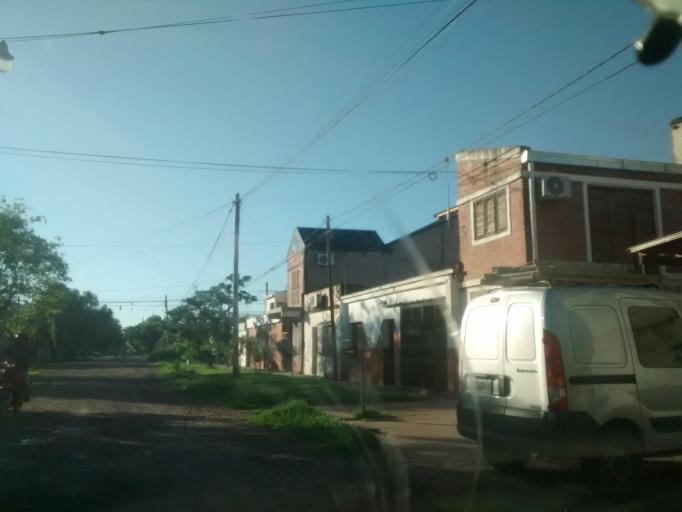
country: AR
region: Chaco
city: Resistencia
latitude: -27.4451
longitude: -59.0039
